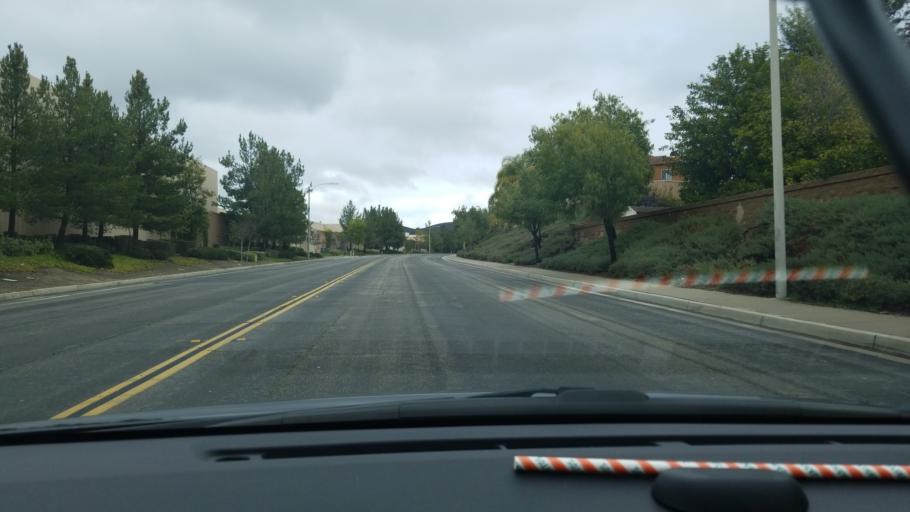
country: US
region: California
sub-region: Riverside County
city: Murrieta Hot Springs
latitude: 33.5696
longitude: -117.1790
